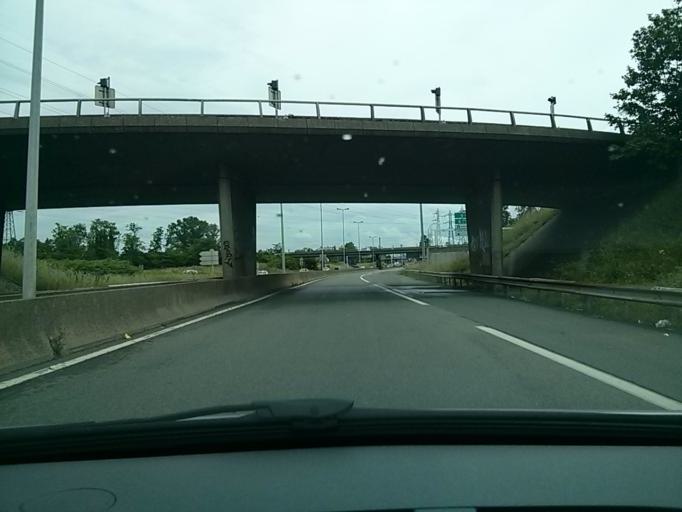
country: FR
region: Rhone-Alpes
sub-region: Departement du Rhone
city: Saint-Fons
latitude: 45.7164
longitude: 4.8428
